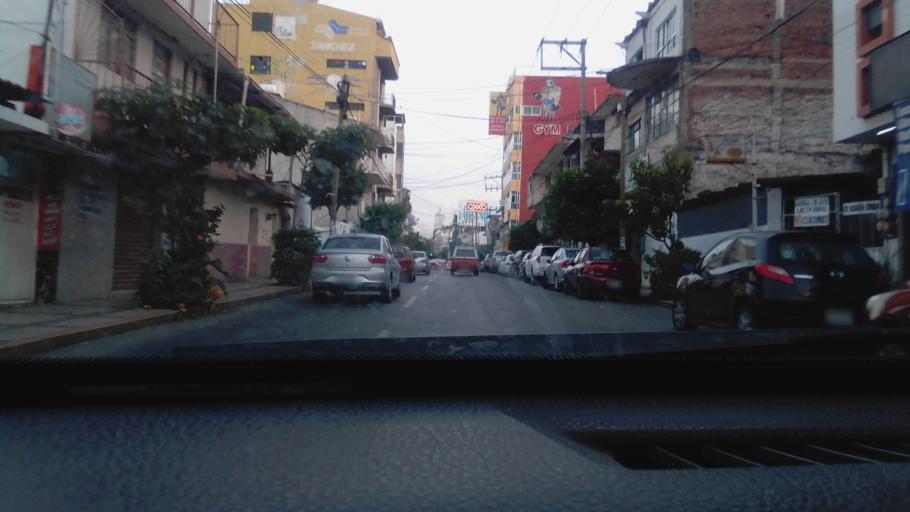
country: MX
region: Guerrero
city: Chilpancingo de los Bravos
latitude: 17.5495
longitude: -99.4991
